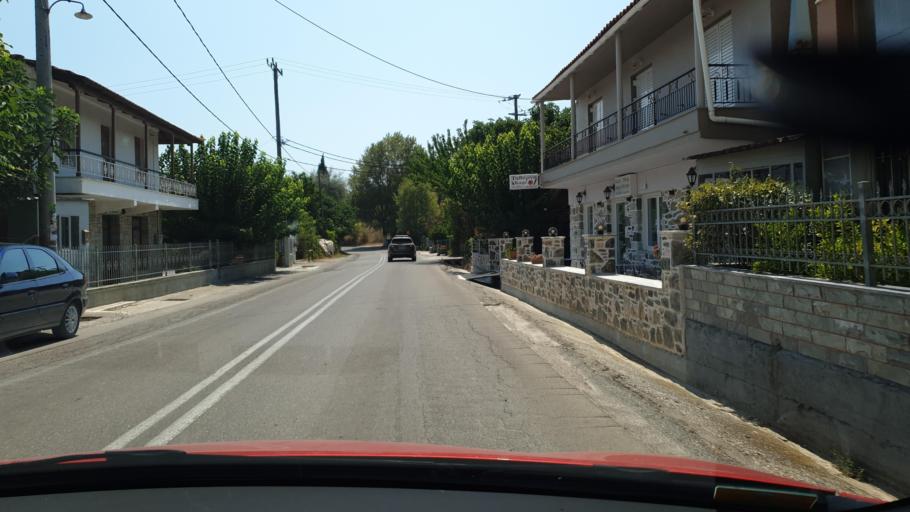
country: GR
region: Central Greece
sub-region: Nomos Evvoias
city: Aliveri
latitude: 38.4661
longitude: 24.1165
